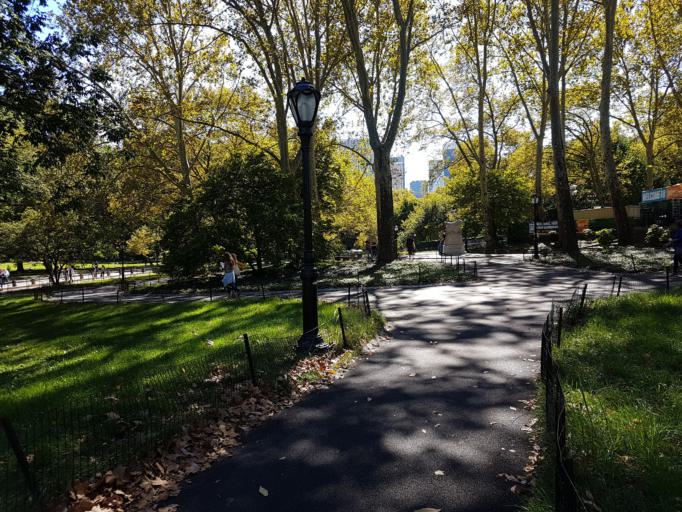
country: US
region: New York
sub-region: New York County
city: Manhattan
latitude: 40.7728
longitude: -73.9694
